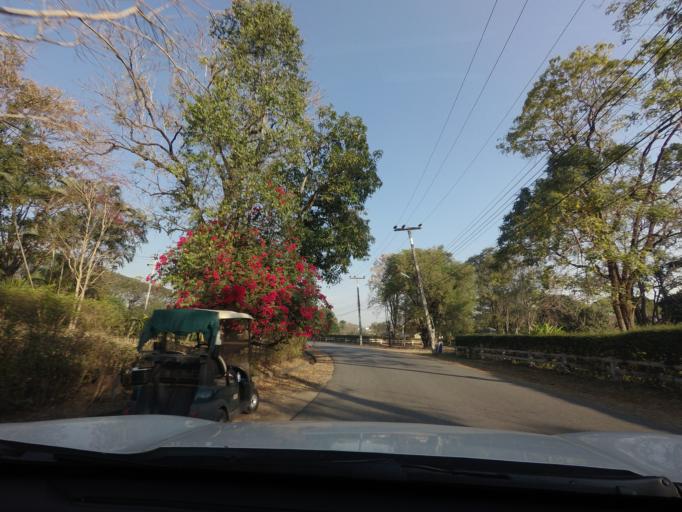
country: TH
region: Nakhon Ratchasima
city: Pak Chong
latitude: 14.5870
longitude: 101.4450
